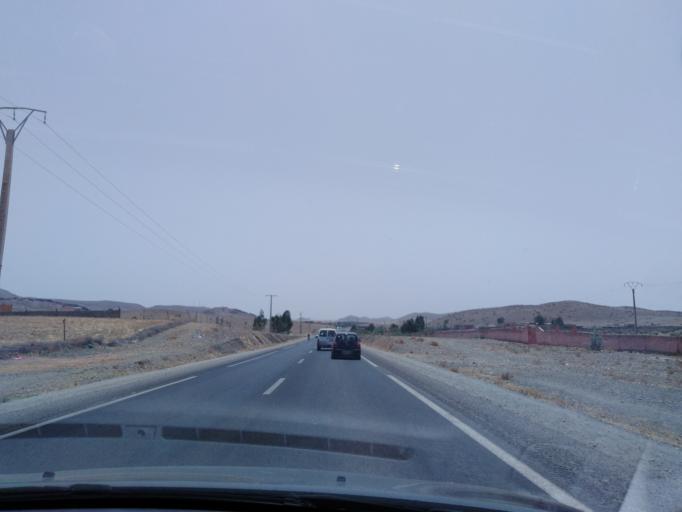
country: MA
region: Marrakech-Tensift-Al Haouz
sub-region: Kelaa-Des-Sraghna
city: Sidi Bou Othmane
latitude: 31.8778
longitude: -8.1889
